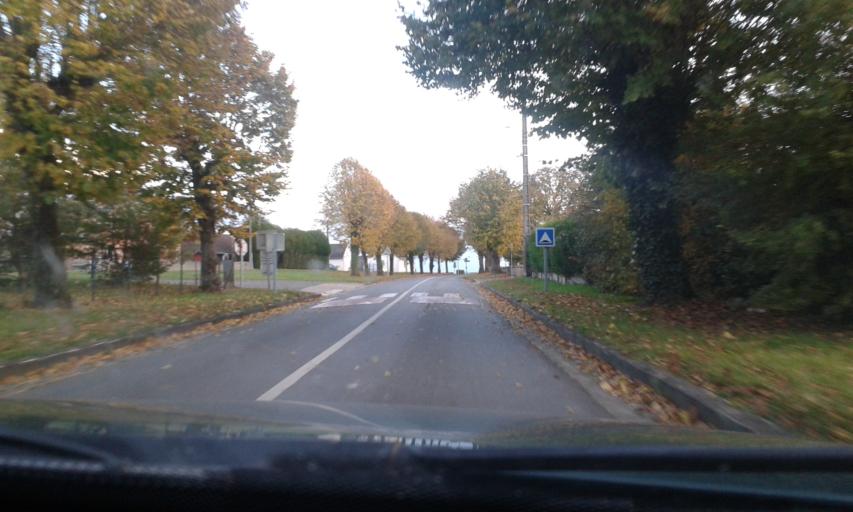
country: FR
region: Centre
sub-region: Departement du Loiret
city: Bricy
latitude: 47.9805
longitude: 1.7819
